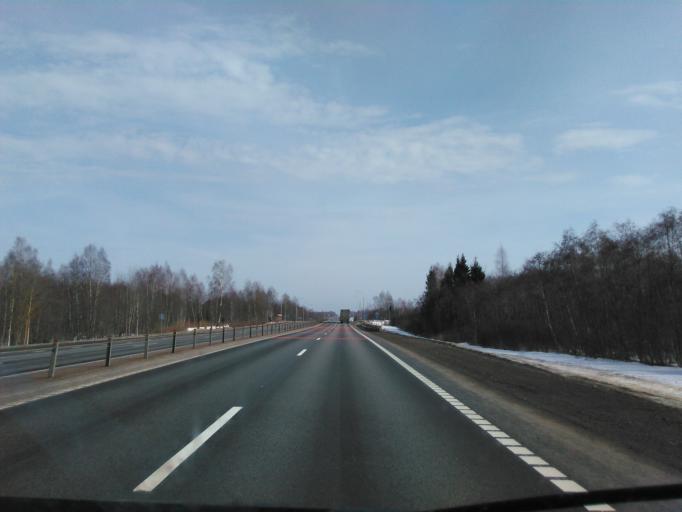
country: BY
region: Vitebsk
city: Dubrowna
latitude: 54.6899
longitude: 30.9269
